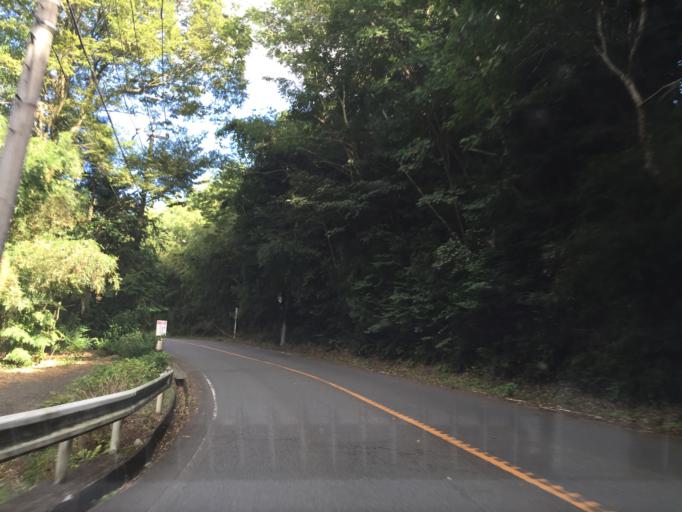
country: JP
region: Shizuoka
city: Mishima
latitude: 35.1650
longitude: 138.9284
